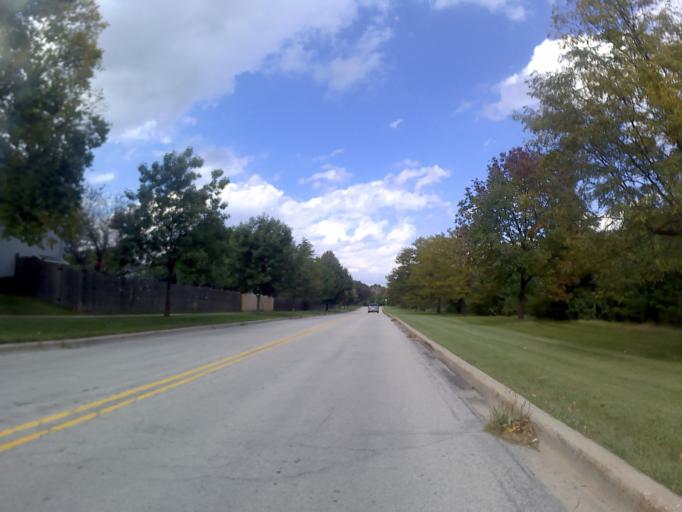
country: US
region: Illinois
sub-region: Will County
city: Bolingbrook
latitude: 41.7333
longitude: -88.0983
